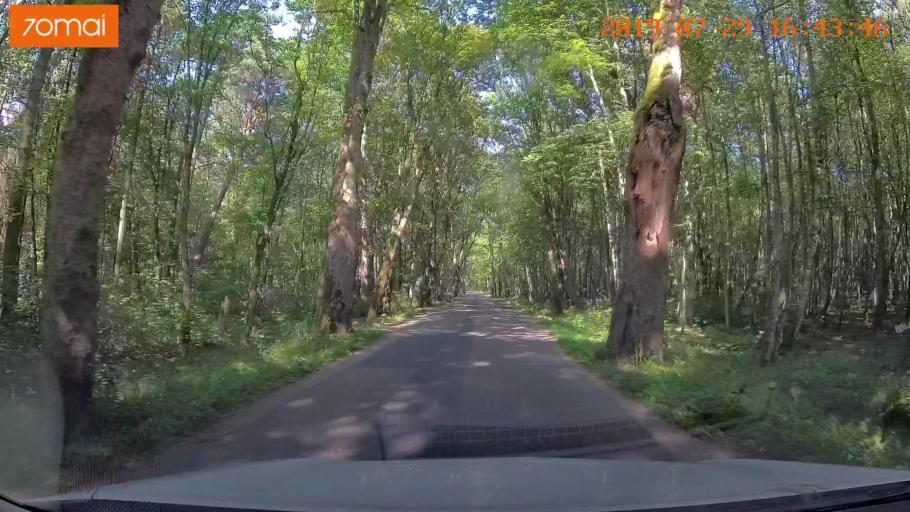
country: RU
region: Kaliningrad
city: Primorsk
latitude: 54.7509
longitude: 20.0882
